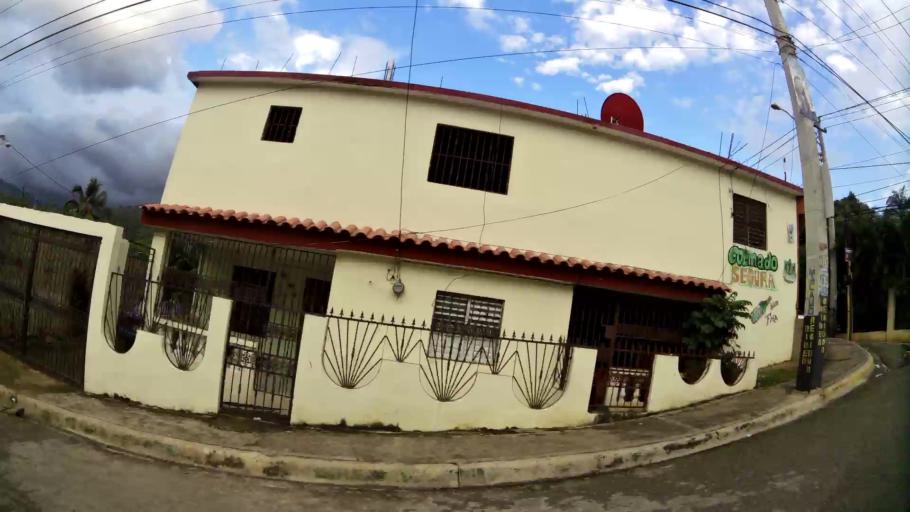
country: DO
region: San Cristobal
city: Villa Altagracia
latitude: 18.6694
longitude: -70.1703
